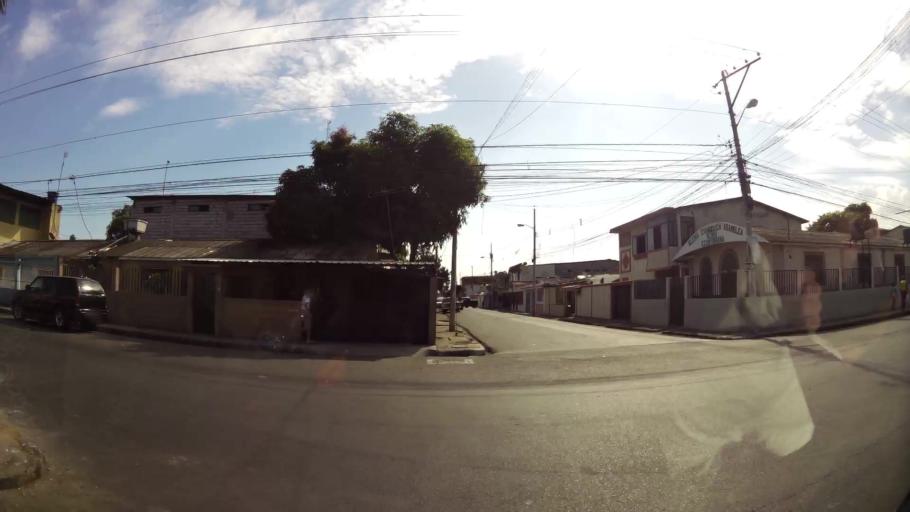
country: EC
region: Guayas
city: Guayaquil
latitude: -2.2073
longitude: -79.9120
